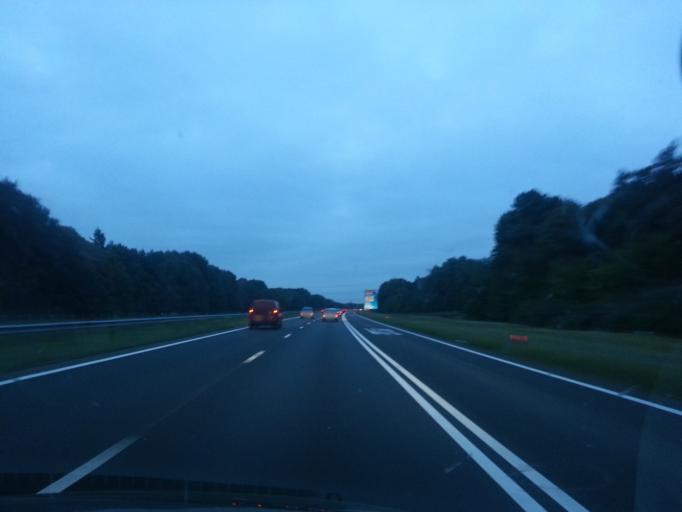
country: NL
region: North Brabant
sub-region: Gemeente Loon op Zand
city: Loon op Zand
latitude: 51.6110
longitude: 5.0709
